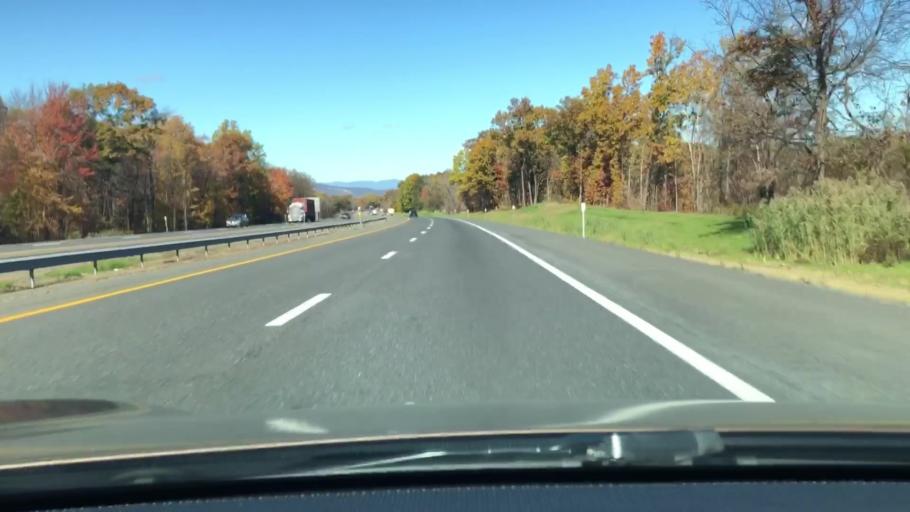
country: US
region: New York
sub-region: Ulster County
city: Clintondale
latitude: 41.6663
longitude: -74.0783
